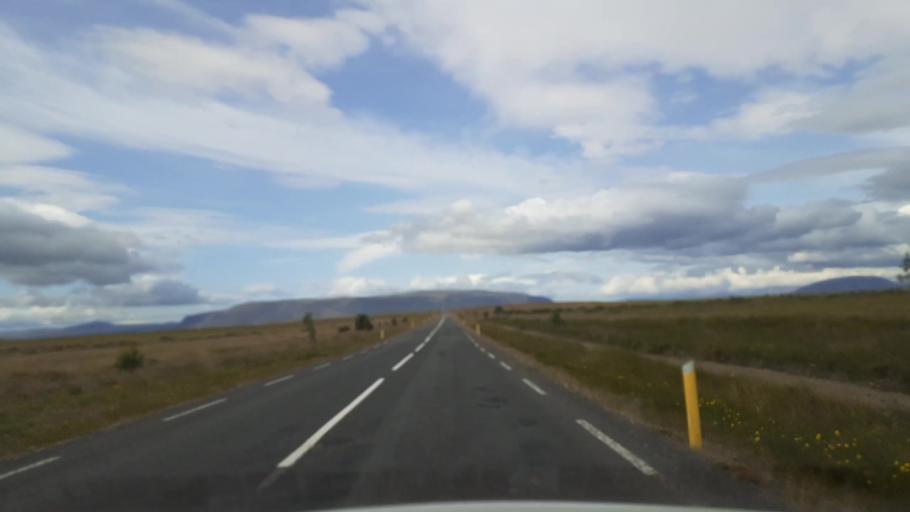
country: IS
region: South
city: Selfoss
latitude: 63.9109
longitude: -20.8291
